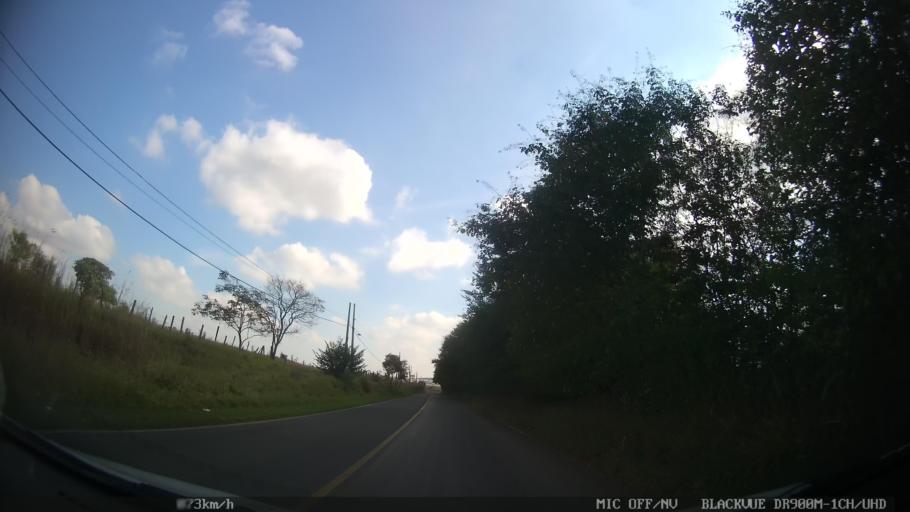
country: BR
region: Sao Paulo
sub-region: Indaiatuba
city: Indaiatuba
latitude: -22.9864
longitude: -47.1767
